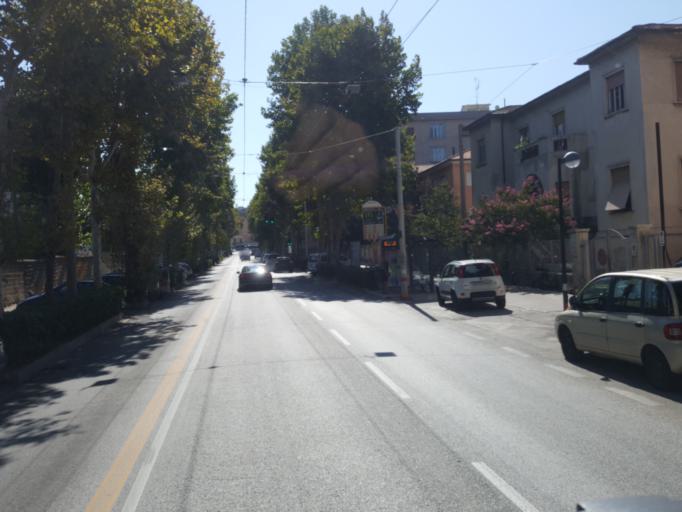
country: IT
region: The Marches
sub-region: Provincia di Ancona
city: Ancona
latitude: 43.6055
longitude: 13.5036
